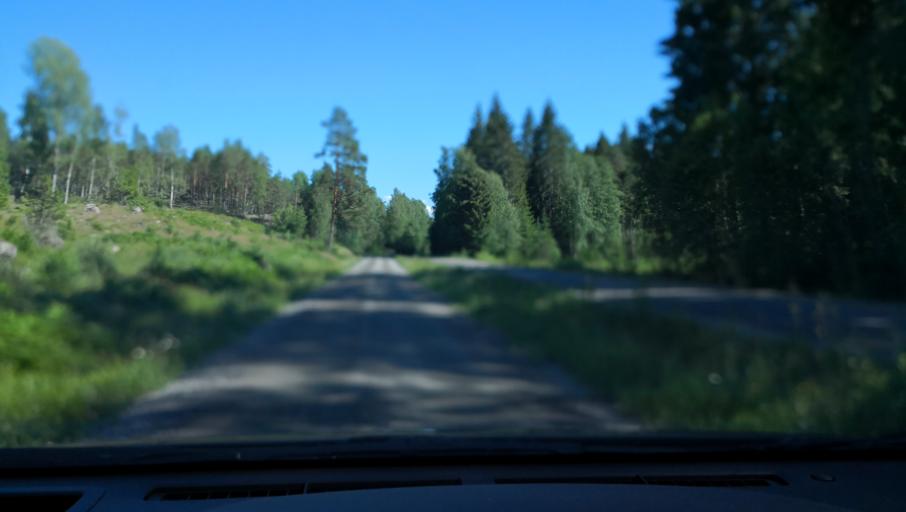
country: SE
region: Soedermanland
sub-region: Eskilstuna Kommun
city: Eskilstuna
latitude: 59.3319
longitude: 16.5786
